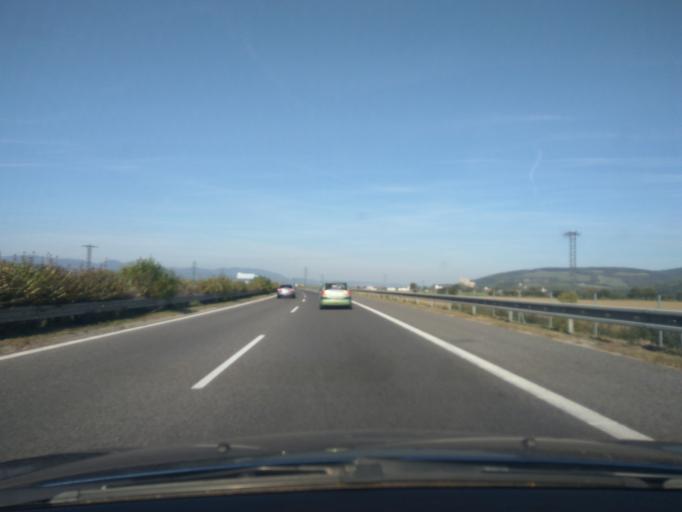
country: SK
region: Trenciansky
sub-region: Okres Nove Mesto nad Vahom
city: Nove Mesto nad Vahom
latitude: 48.7703
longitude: 17.8754
